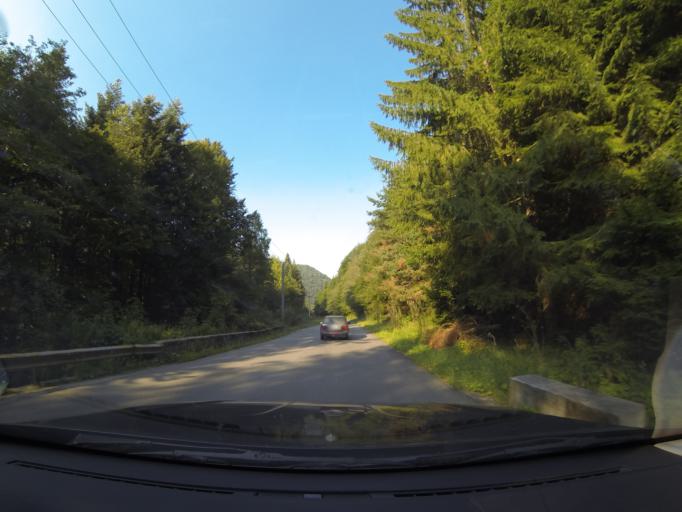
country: RO
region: Arges
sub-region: Comuna Arefu
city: Arefu
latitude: 45.4009
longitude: 24.6416
